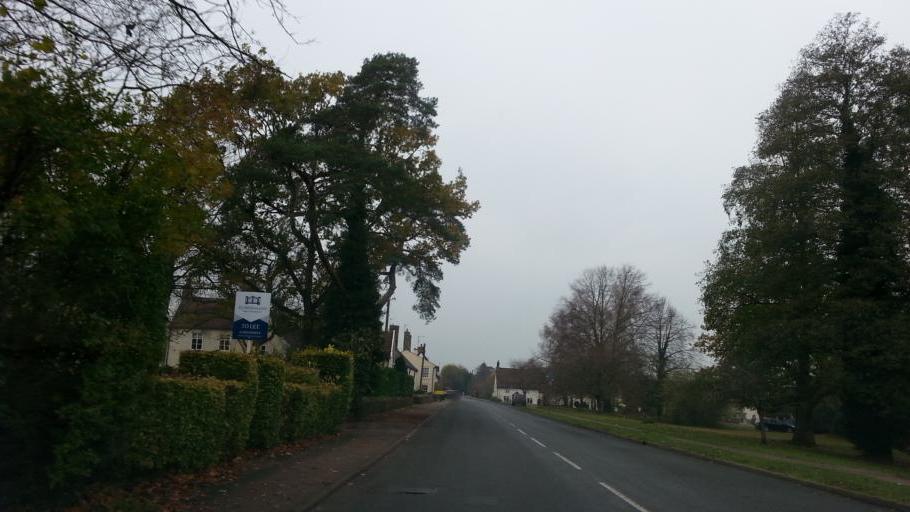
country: GB
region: England
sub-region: Suffolk
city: Thurston
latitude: 52.2342
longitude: 0.8334
